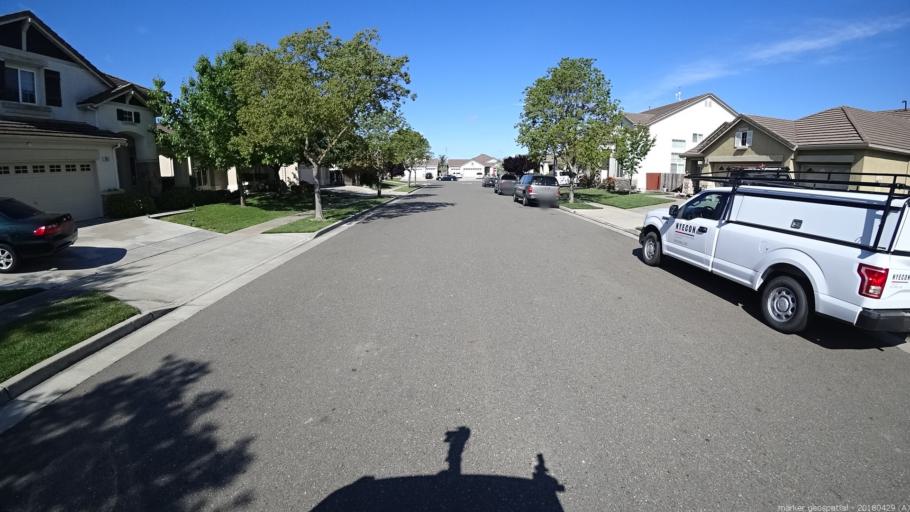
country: US
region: California
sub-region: Yolo County
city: West Sacramento
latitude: 38.5376
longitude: -121.5802
